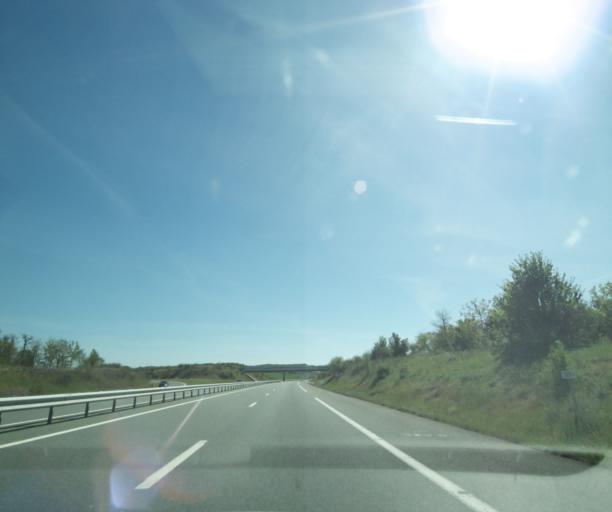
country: FR
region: Midi-Pyrenees
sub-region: Departement du Lot
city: Le Vigan
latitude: 44.7003
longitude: 1.5731
